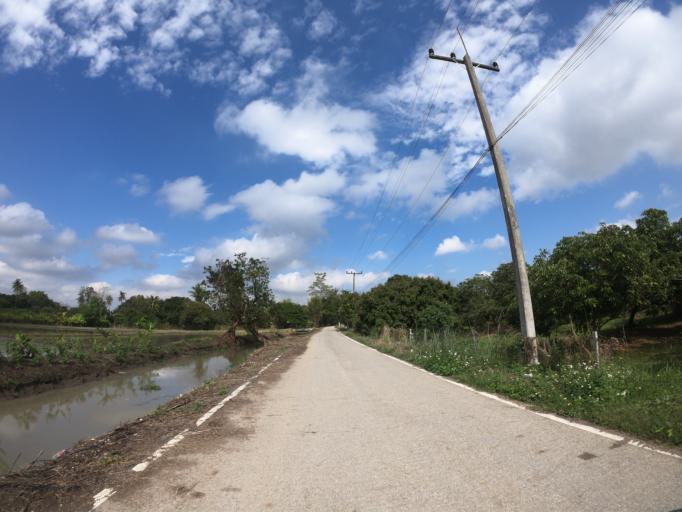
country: TH
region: Chiang Mai
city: Hang Dong
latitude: 18.6963
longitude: 98.9772
